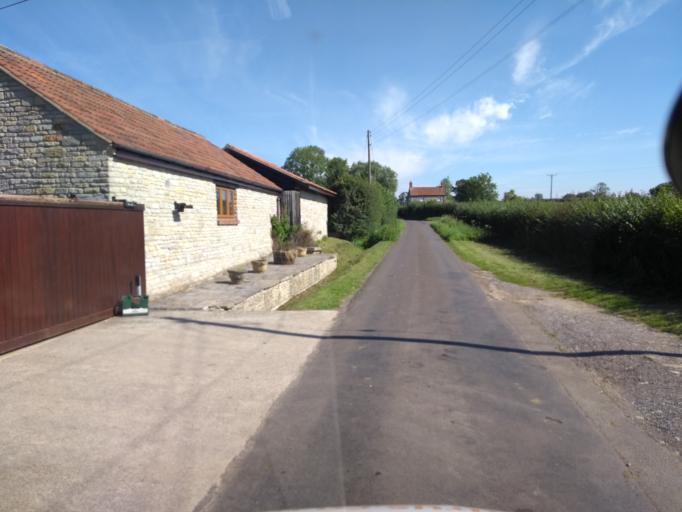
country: GB
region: England
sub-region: Somerset
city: Glastonbury
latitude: 51.1016
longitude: -2.6426
